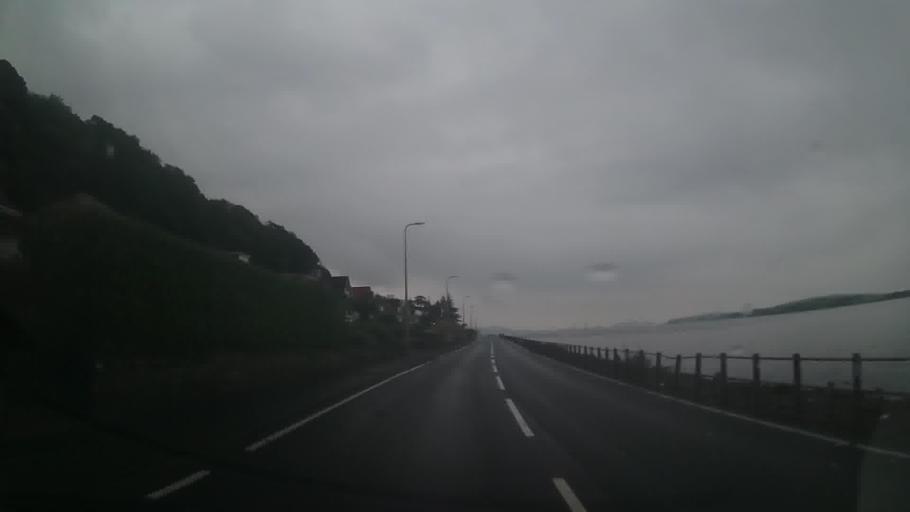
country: GB
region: Scotland
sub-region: North Ayrshire
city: Largs
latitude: 55.8139
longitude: -4.8844
